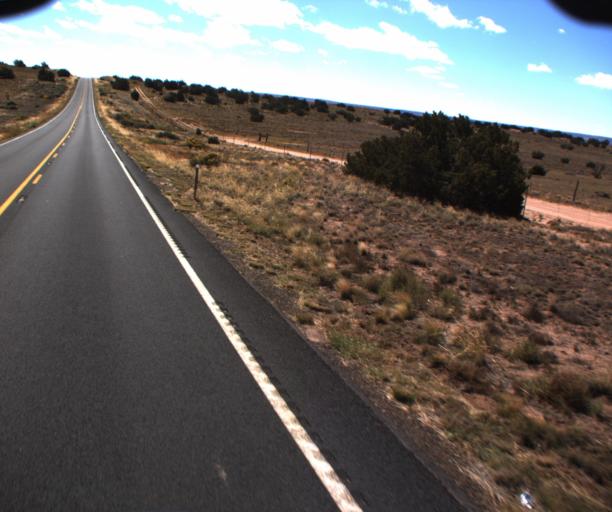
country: US
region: Arizona
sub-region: Apache County
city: Houck
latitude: 35.1229
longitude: -109.3257
